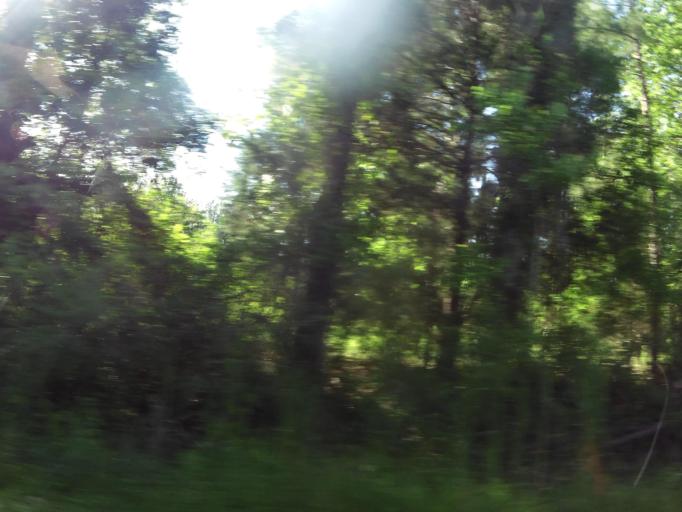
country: US
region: Florida
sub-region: Nassau County
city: Nassau Village-Ratliff
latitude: 30.4899
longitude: -81.8273
